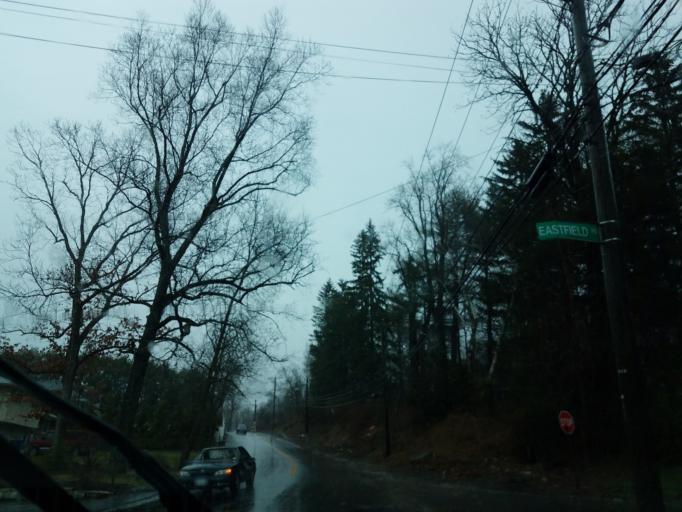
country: US
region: Connecticut
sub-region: New Haven County
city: Waterbury
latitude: 41.5422
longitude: -73.0736
